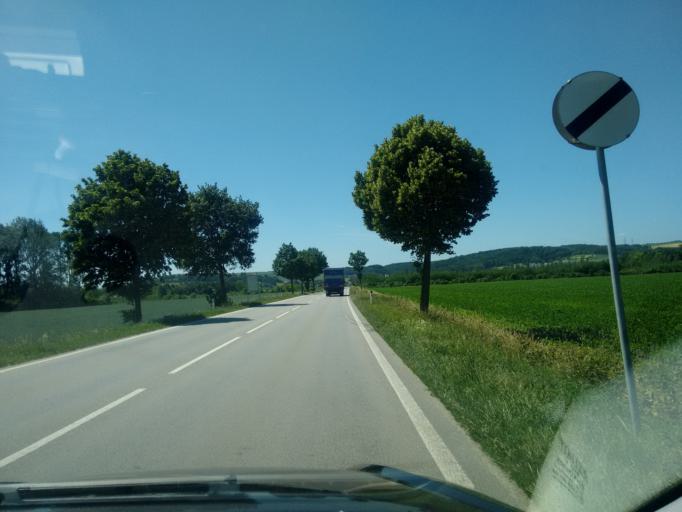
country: AT
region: Lower Austria
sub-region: Politischer Bezirk Sankt Polten
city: Hafnerbach
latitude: 48.1976
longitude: 15.4787
